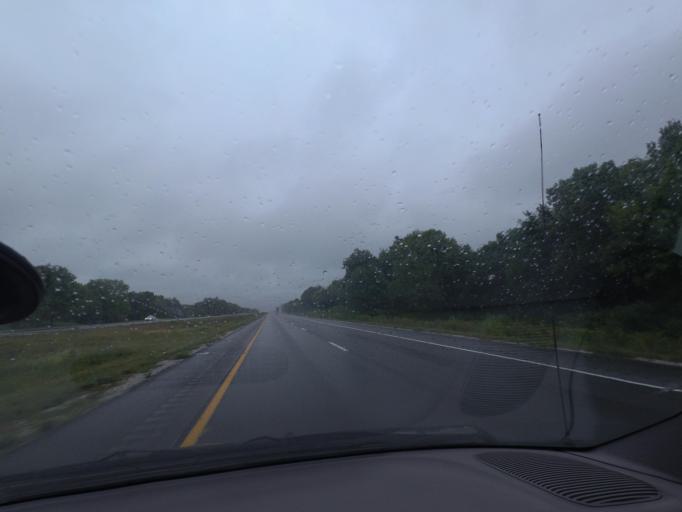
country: US
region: Illinois
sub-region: Scott County
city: Winchester
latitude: 39.6811
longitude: -90.4992
